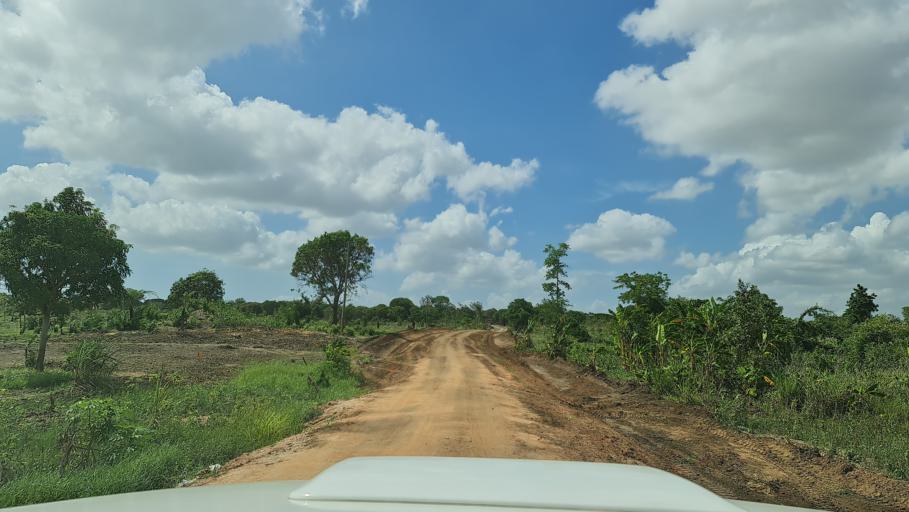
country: MZ
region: Nampula
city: Ilha de Mocambique
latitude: -15.0126
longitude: 40.5604
